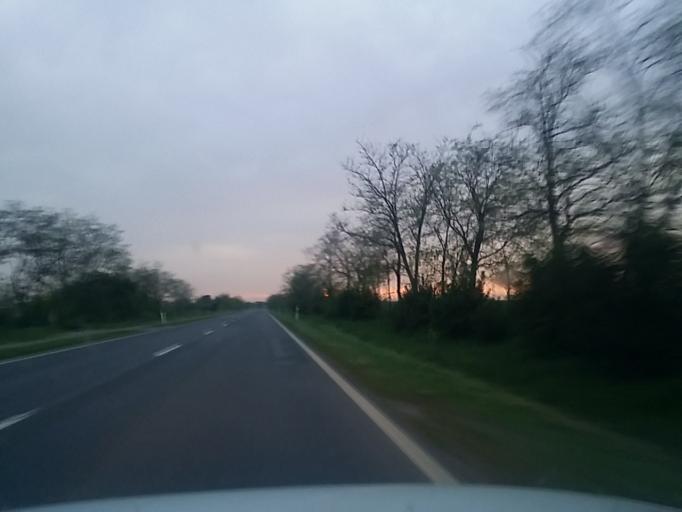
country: HU
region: Bekes
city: Mezobereny
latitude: 46.7125
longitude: 20.9558
